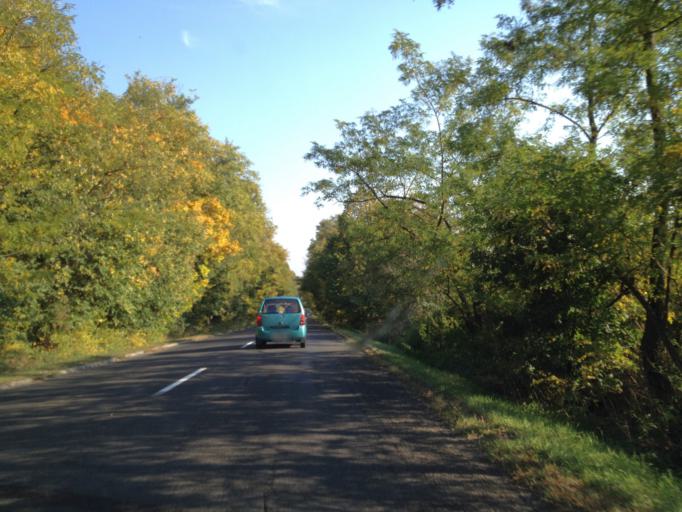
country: HU
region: Pest
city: Pilisszentkereszt
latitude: 47.6837
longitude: 18.9302
